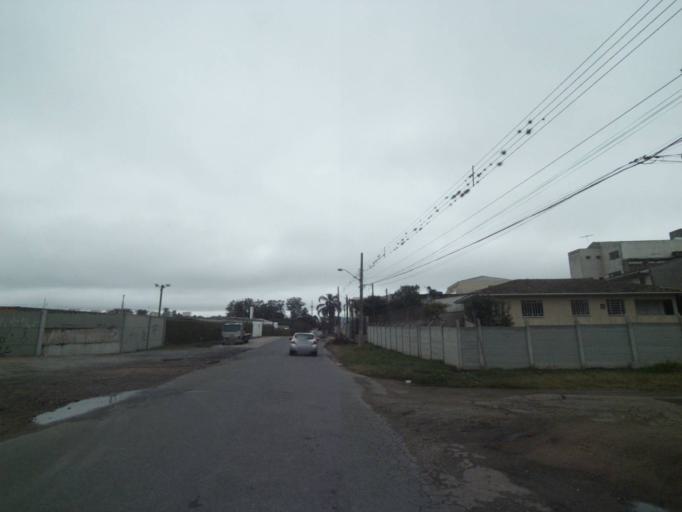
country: BR
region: Parana
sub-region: Curitiba
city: Curitiba
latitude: -25.5075
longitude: -49.2952
